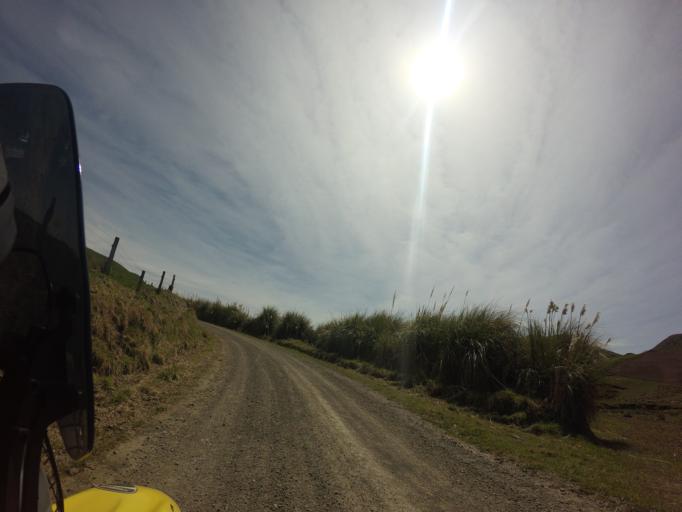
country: NZ
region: Bay of Plenty
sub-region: Opotiki District
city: Opotiki
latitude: -38.4599
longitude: 177.3799
